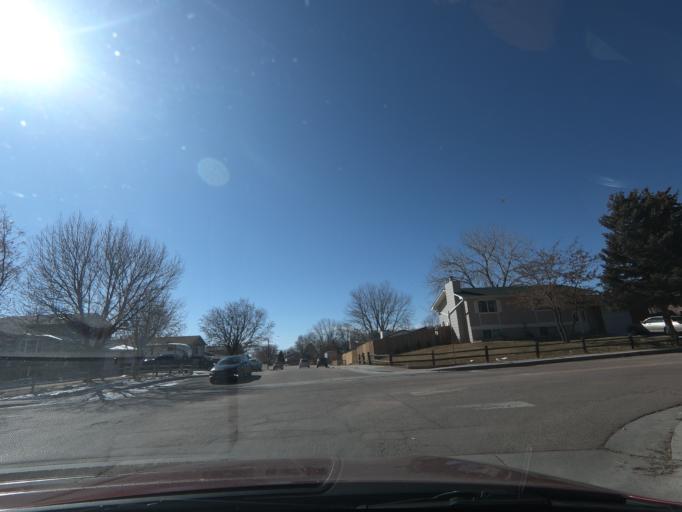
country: US
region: Colorado
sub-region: El Paso County
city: Security-Widefield
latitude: 38.7305
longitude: -104.6856
